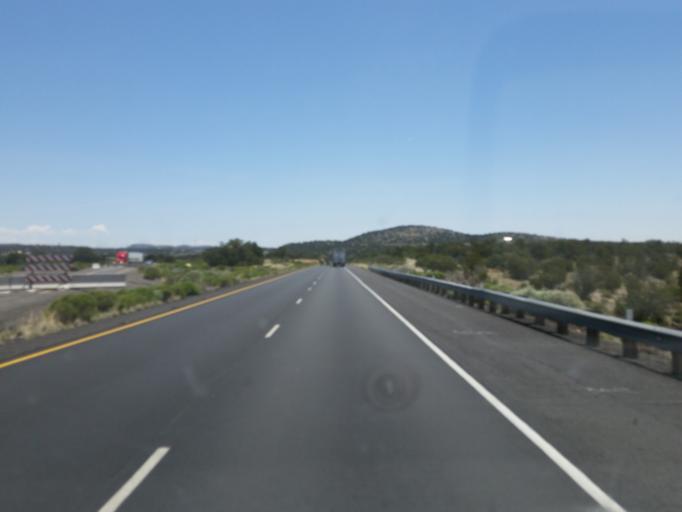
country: US
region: Arizona
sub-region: Coconino County
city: Flagstaff
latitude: 35.2014
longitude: -111.4357
